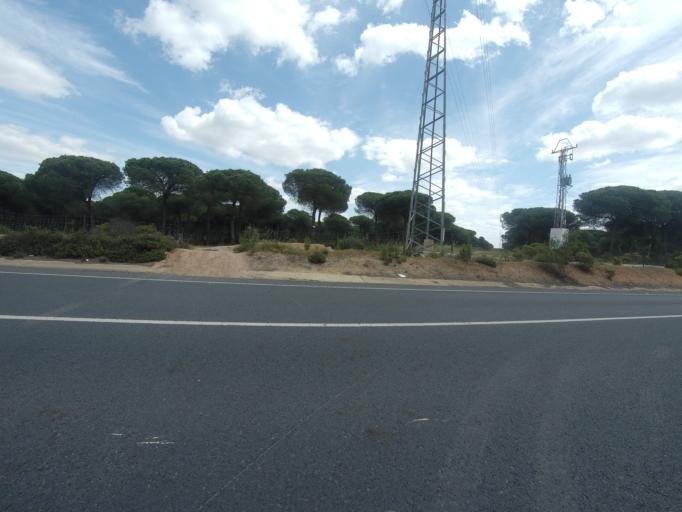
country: ES
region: Andalusia
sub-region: Provincia de Huelva
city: Aljaraque
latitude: 37.2263
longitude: -7.0599
